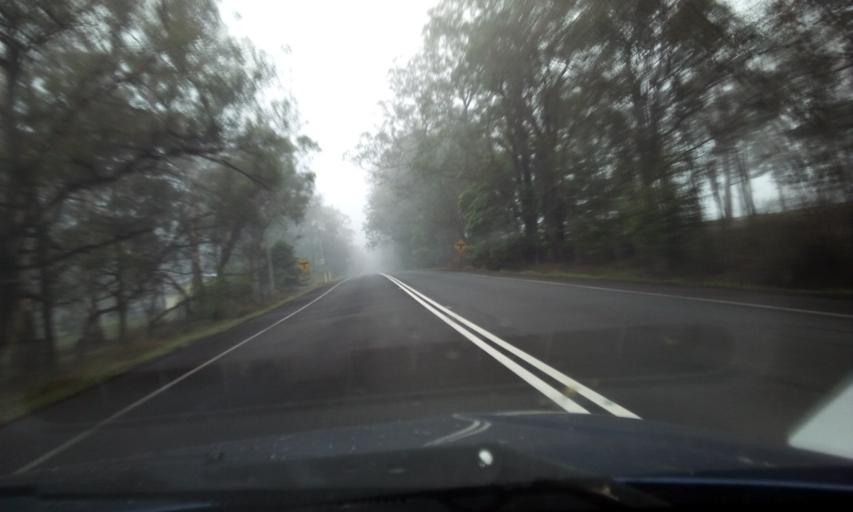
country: AU
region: New South Wales
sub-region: Wollondilly
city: Douglas Park
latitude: -34.2432
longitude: 150.7276
